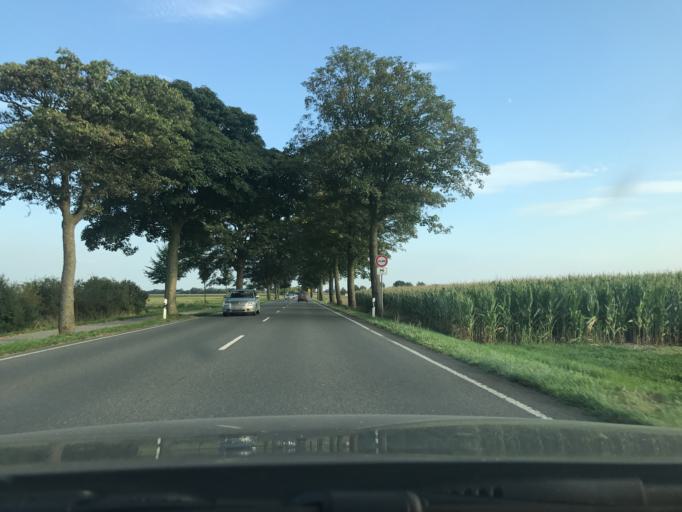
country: DE
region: North Rhine-Westphalia
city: Geldern
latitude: 51.4714
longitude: 6.3536
